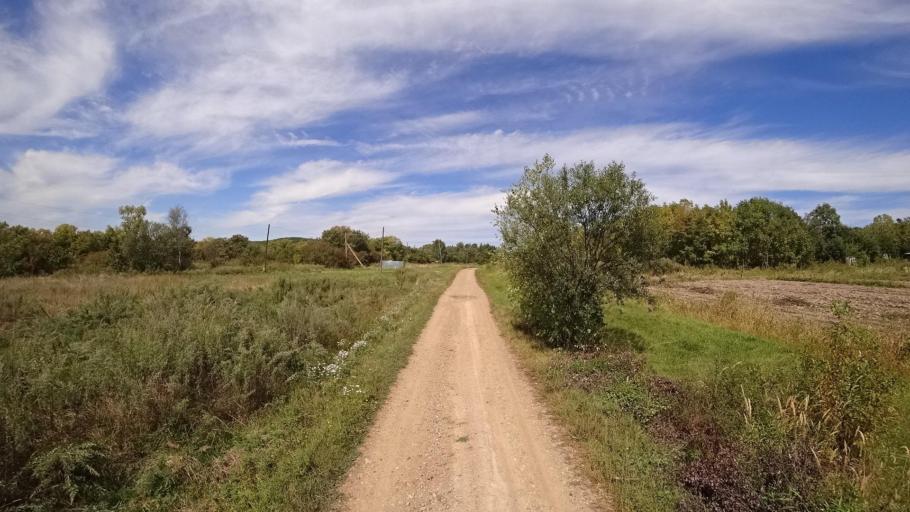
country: RU
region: Primorskiy
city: Yakovlevka
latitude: 44.6470
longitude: 133.5880
